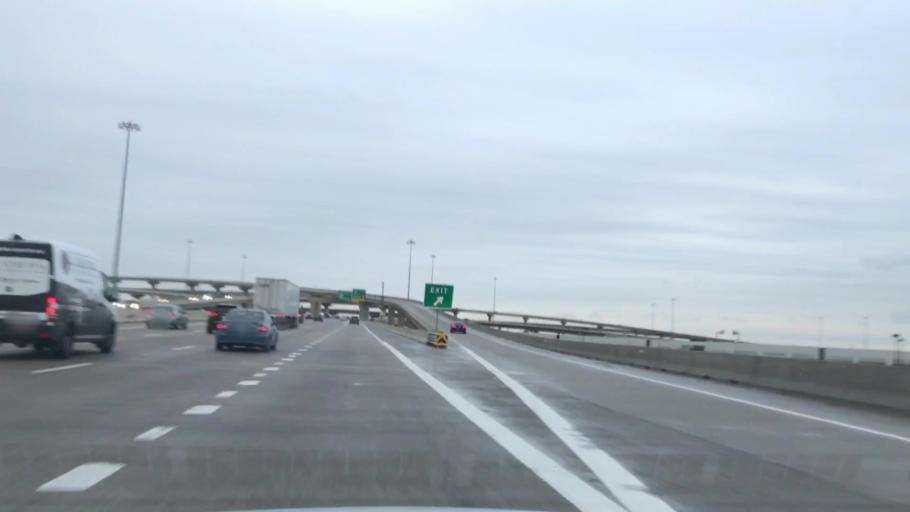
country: US
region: Texas
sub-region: Denton County
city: Lewisville
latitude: 32.9957
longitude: -96.9641
